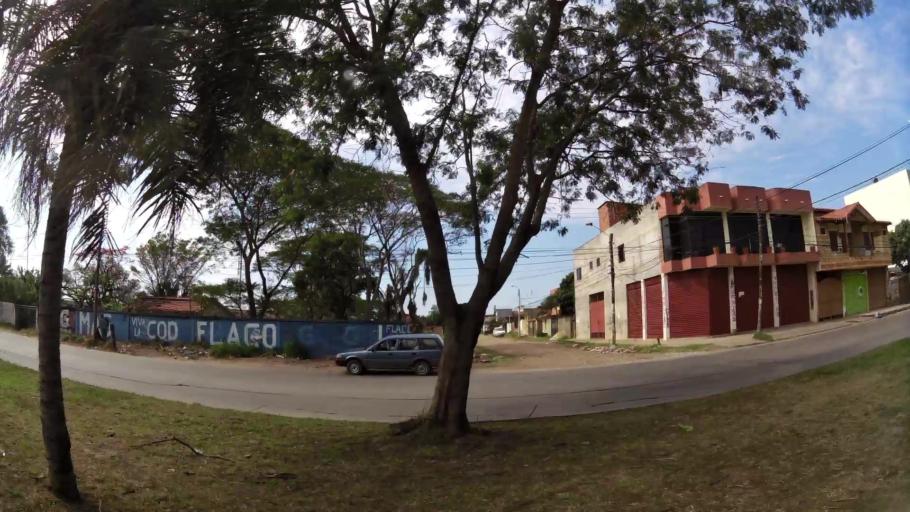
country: BO
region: Santa Cruz
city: Santa Cruz de la Sierra
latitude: -17.7494
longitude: -63.1538
